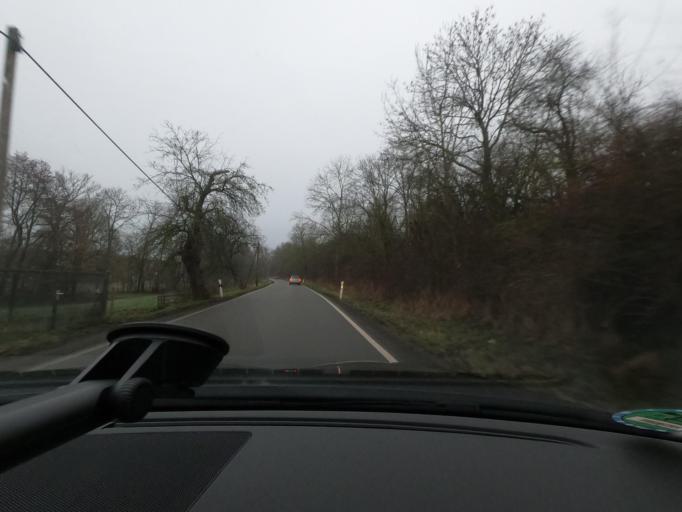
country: DE
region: Thuringia
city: Dornheim
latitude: 50.8120
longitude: 11.0095
